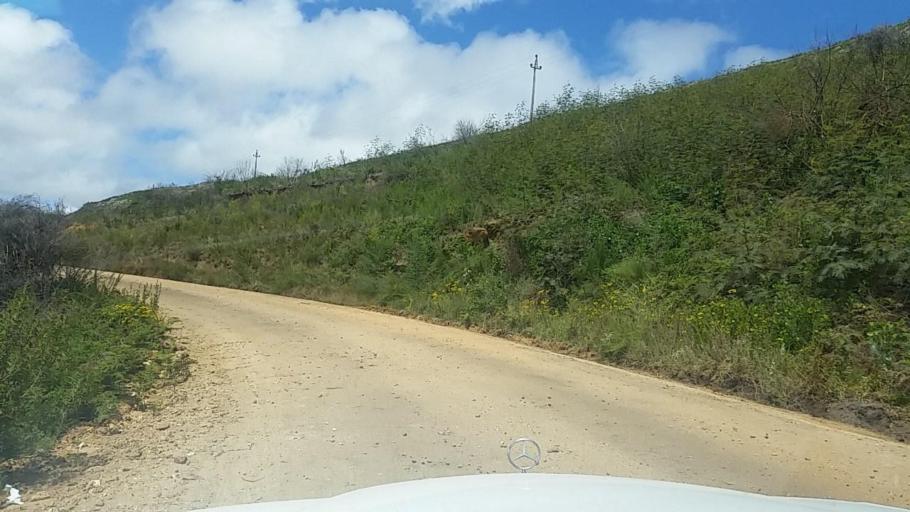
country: ZA
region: Western Cape
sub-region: Eden District Municipality
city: Knysna
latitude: -33.8869
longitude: 23.1607
